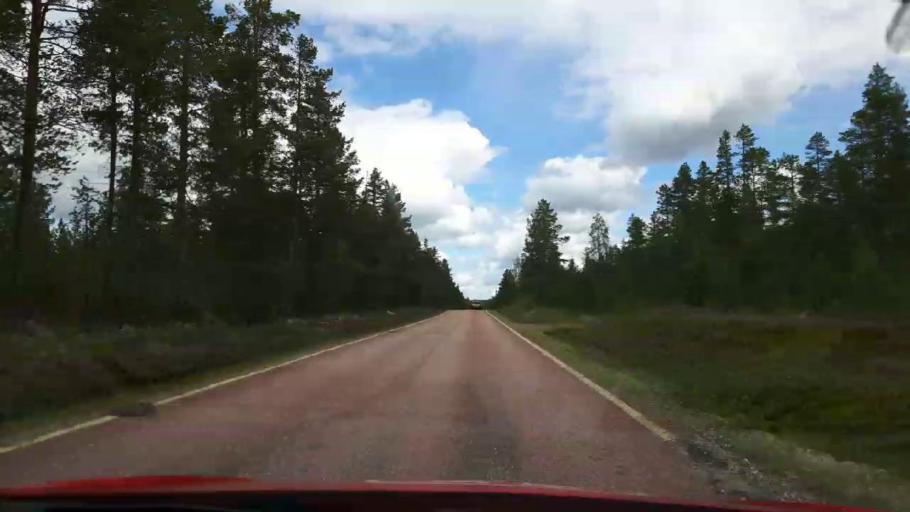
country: NO
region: Hedmark
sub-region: Trysil
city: Innbygda
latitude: 61.8846
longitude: 12.9764
